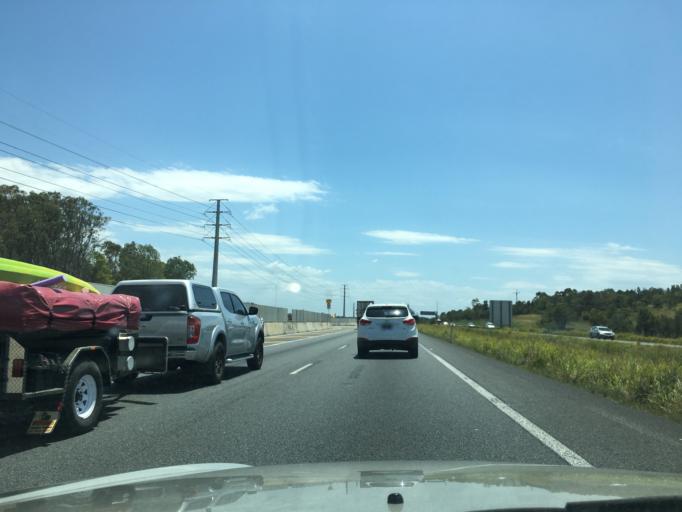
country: AU
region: Queensland
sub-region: Brisbane
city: Shorncliffe
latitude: -27.3635
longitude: 153.0963
